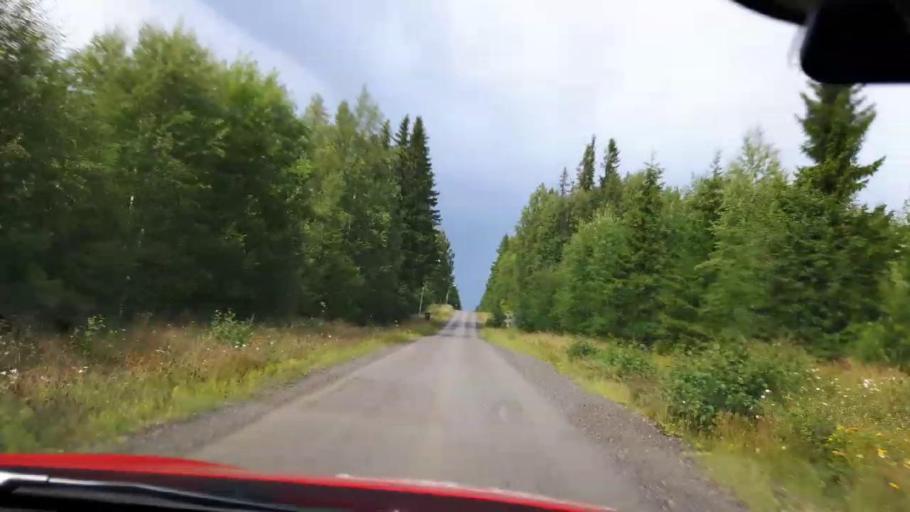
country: SE
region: Jaemtland
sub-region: Stroemsunds Kommun
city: Stroemsund
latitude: 64.0619
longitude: 15.8897
